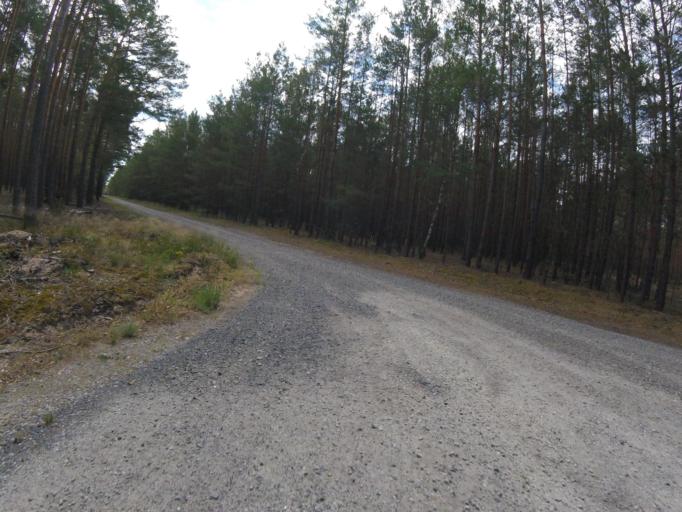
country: DE
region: Brandenburg
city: Schwerin
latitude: 52.1369
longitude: 13.6604
